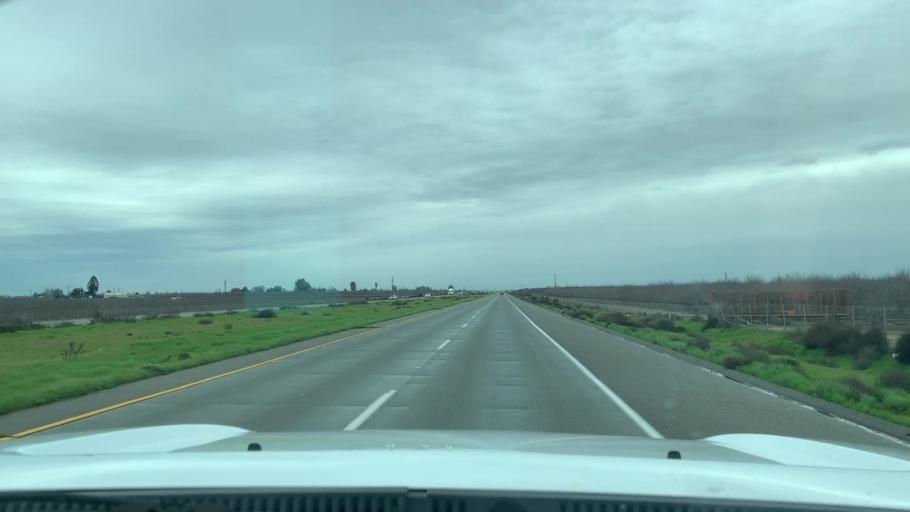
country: US
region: California
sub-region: Fresno County
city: Caruthers
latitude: 36.5325
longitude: -119.7860
